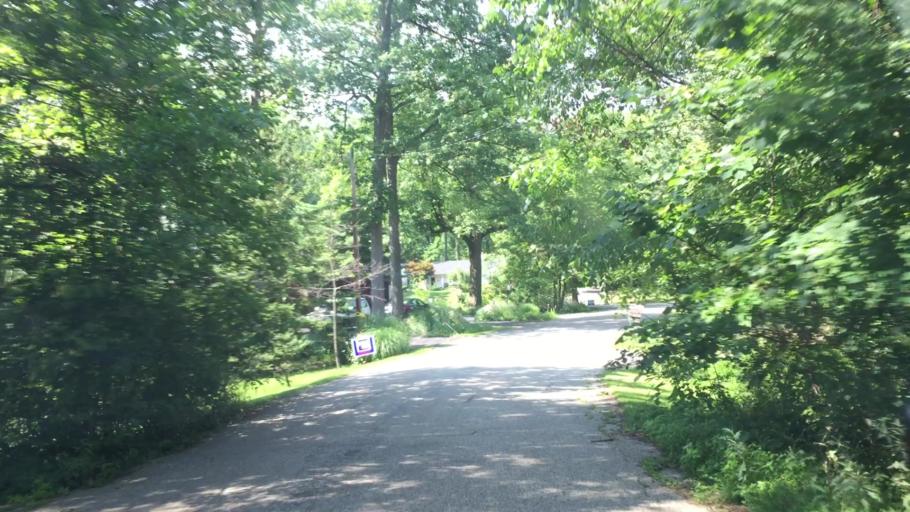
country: US
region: Michigan
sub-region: Oakland County
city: Franklin
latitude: 42.5456
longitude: -83.3109
